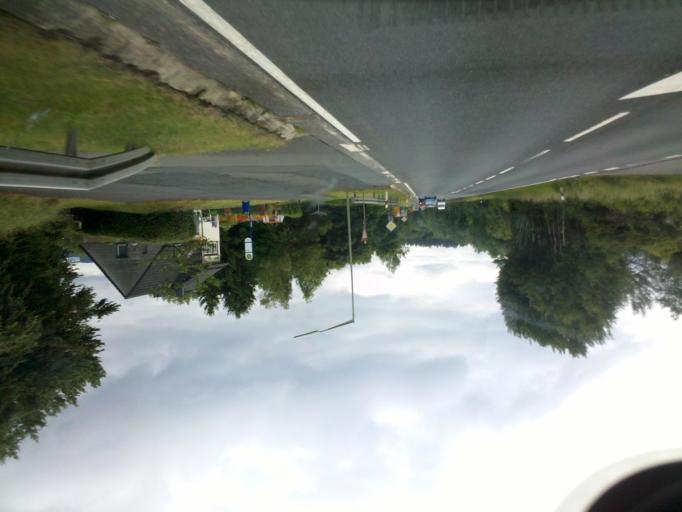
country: DE
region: Hesse
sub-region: Regierungsbezirk Giessen
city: Haiger
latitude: 50.7658
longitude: 8.1563
